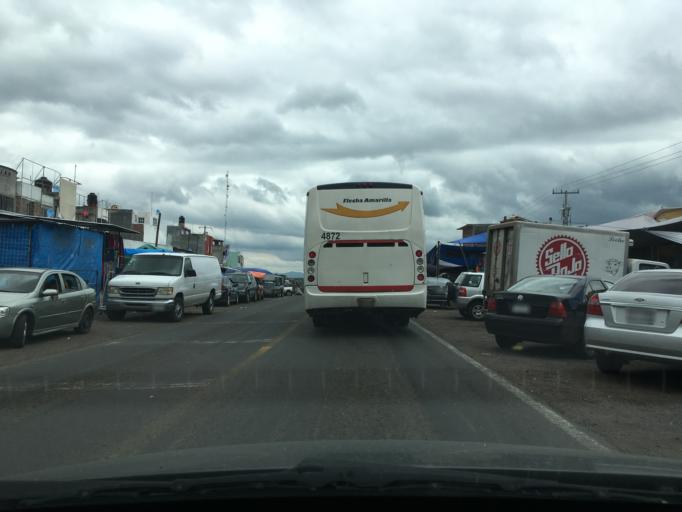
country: MX
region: Michoacan
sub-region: Cuitzeo
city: Cuamio
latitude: 20.0585
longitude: -101.1503
